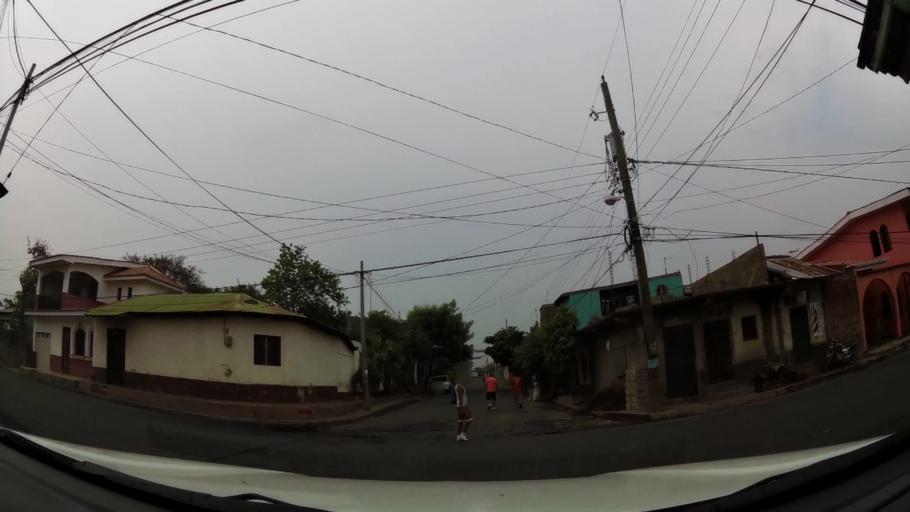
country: NI
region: Leon
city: Leon
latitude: 12.4266
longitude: -86.8799
